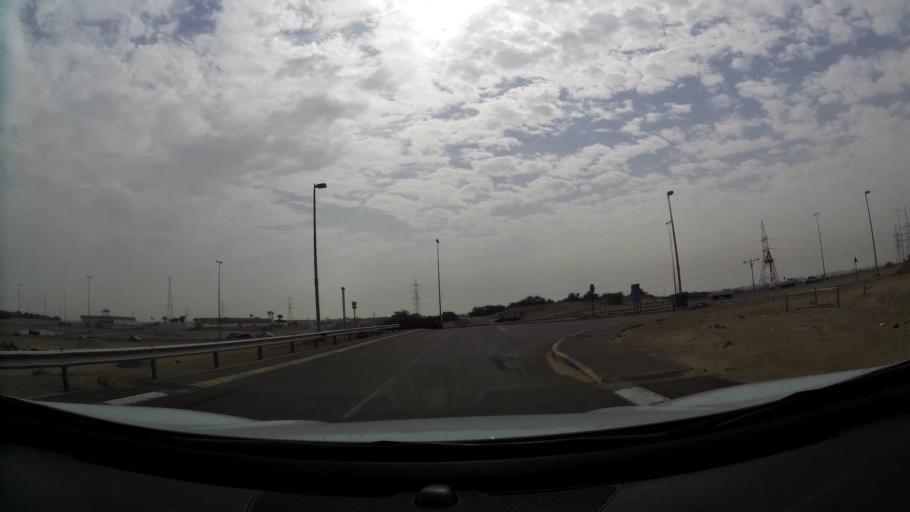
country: AE
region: Abu Dhabi
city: Abu Dhabi
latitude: 24.2994
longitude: 54.6637
